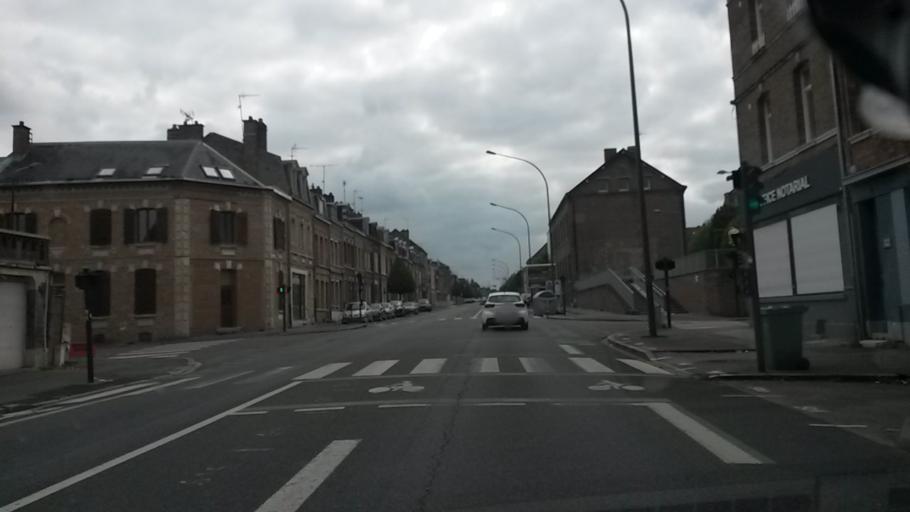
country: FR
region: Picardie
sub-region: Departement de la Somme
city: Amiens
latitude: 49.8907
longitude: 2.2827
